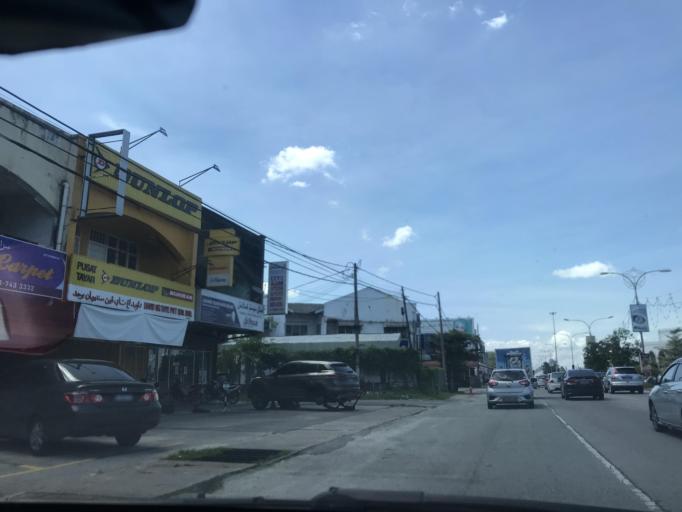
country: MY
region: Kelantan
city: Kota Bharu
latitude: 6.1039
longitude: 102.2617
